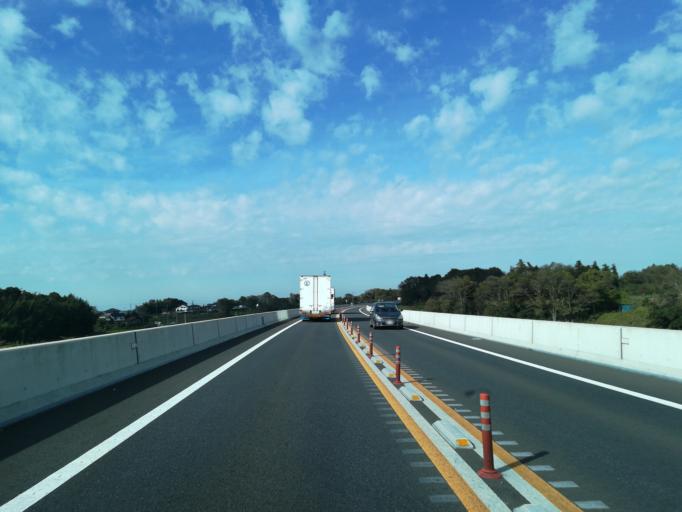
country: JP
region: Ibaraki
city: Mitsukaido
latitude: 36.0694
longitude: 140.0188
